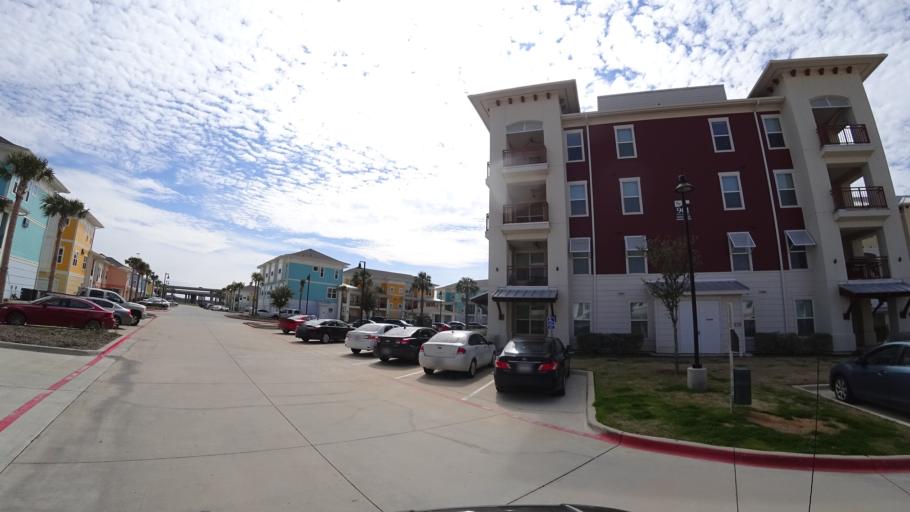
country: US
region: Texas
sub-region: Denton County
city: Lewisville
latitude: 33.0059
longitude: -96.9575
